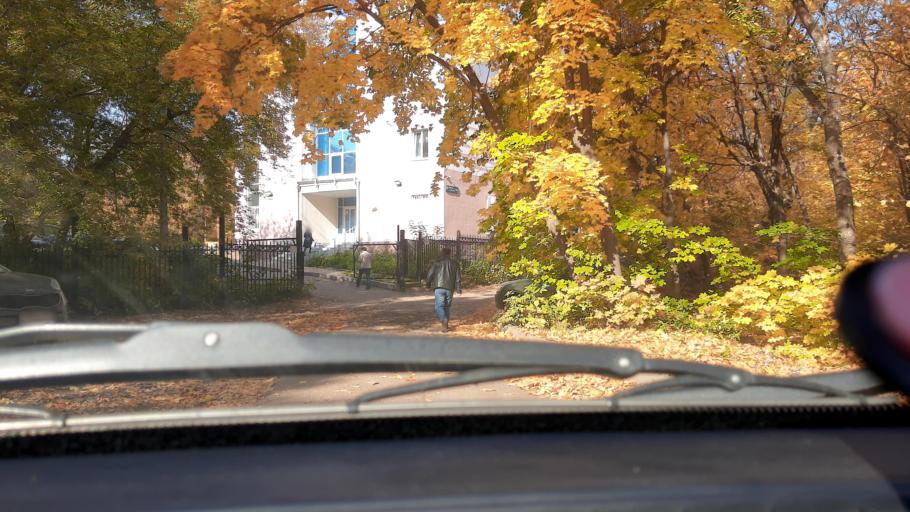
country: RU
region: Bashkortostan
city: Ufa
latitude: 54.7537
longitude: 55.9833
